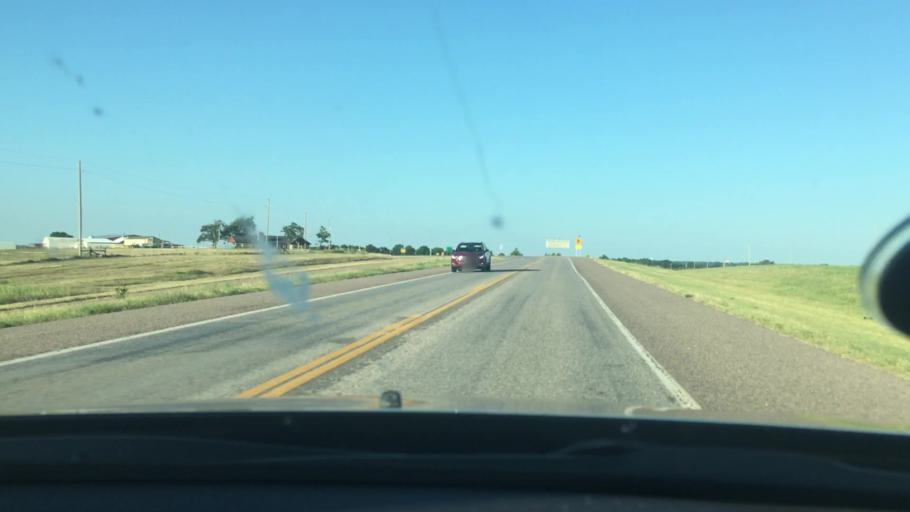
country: US
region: Oklahoma
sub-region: Pontotoc County
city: Ada
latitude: 34.6612
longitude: -96.7925
